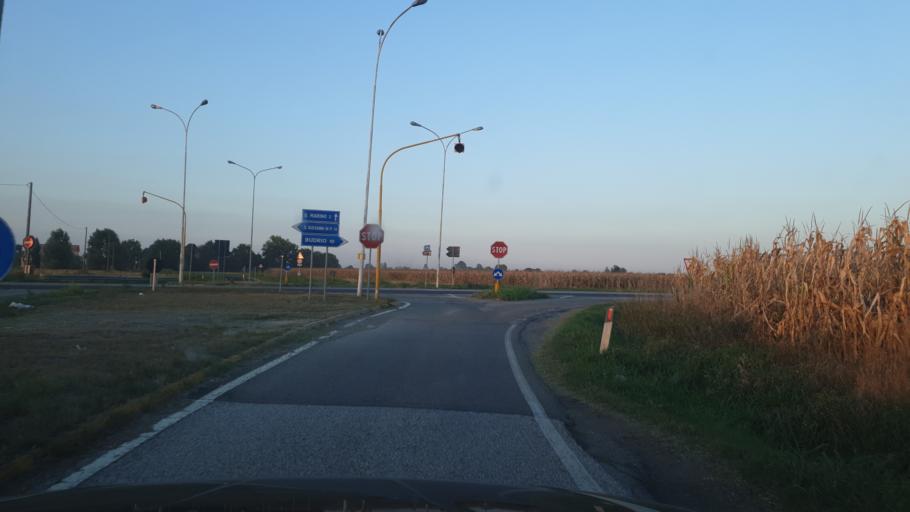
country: IT
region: Emilia-Romagna
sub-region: Provincia di Bologna
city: Progresso
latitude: 44.5844
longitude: 11.4055
